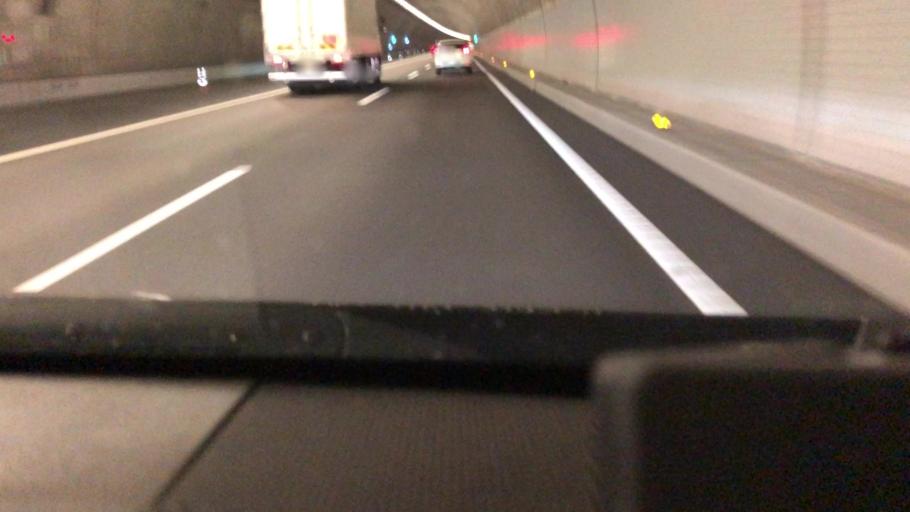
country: JP
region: Shizuoka
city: Kanaya
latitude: 34.8645
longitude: 138.1544
